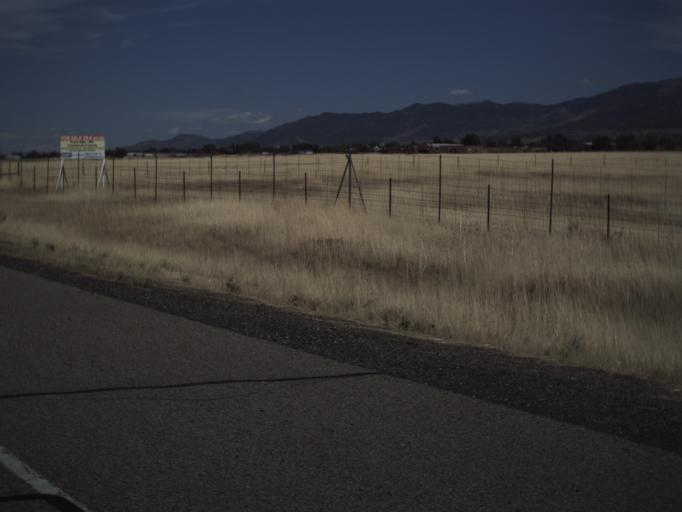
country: US
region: Utah
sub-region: Millard County
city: Fillmore
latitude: 38.9530
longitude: -112.3477
